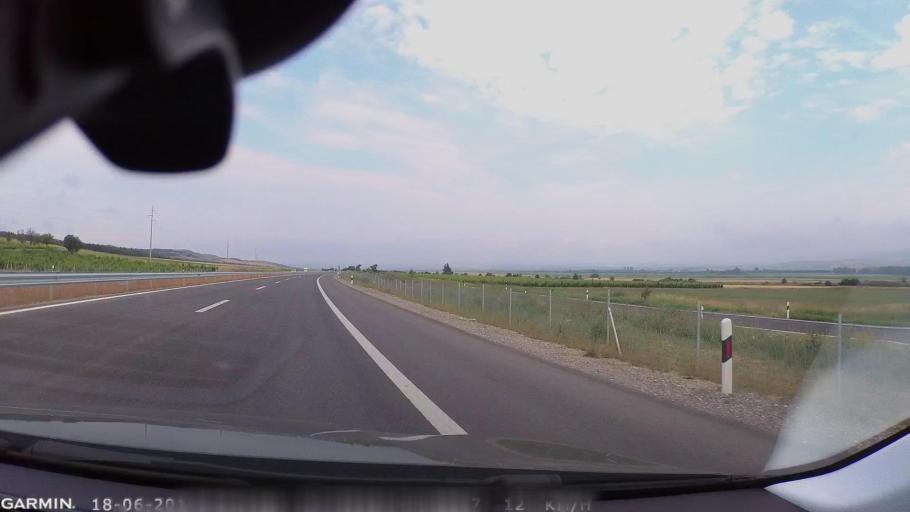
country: MK
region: Stip
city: Shtip
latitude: 41.7917
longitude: 22.0993
